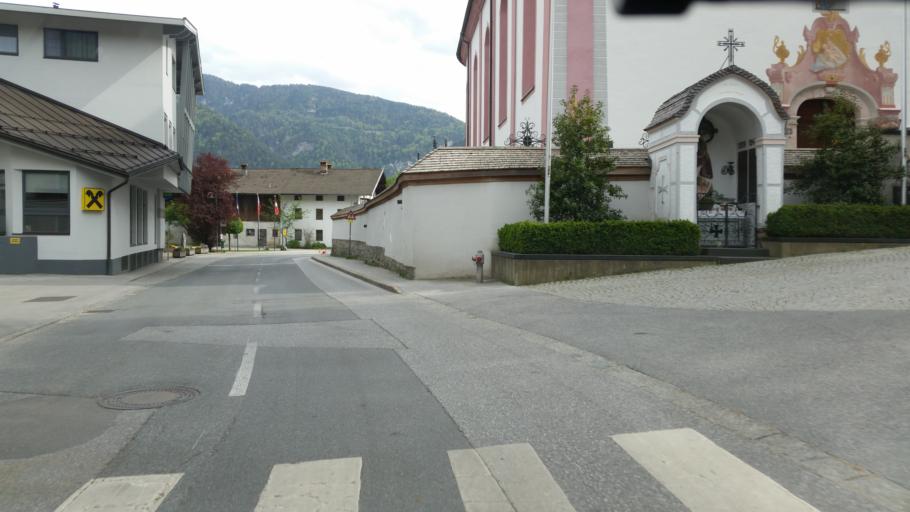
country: AT
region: Tyrol
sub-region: Politischer Bezirk Kufstein
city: Breitenbach am Inn
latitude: 47.4791
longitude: 11.9732
